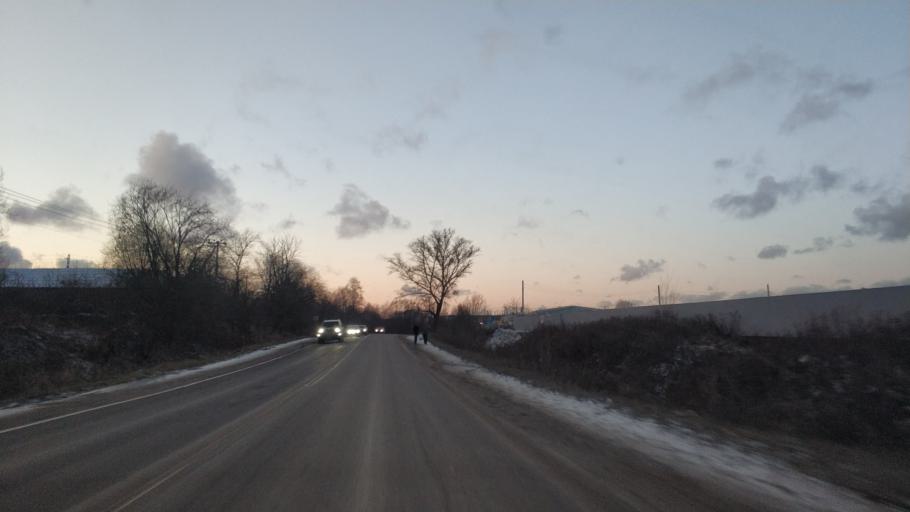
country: RU
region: St.-Petersburg
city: Pontonnyy
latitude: 59.8081
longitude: 30.6166
